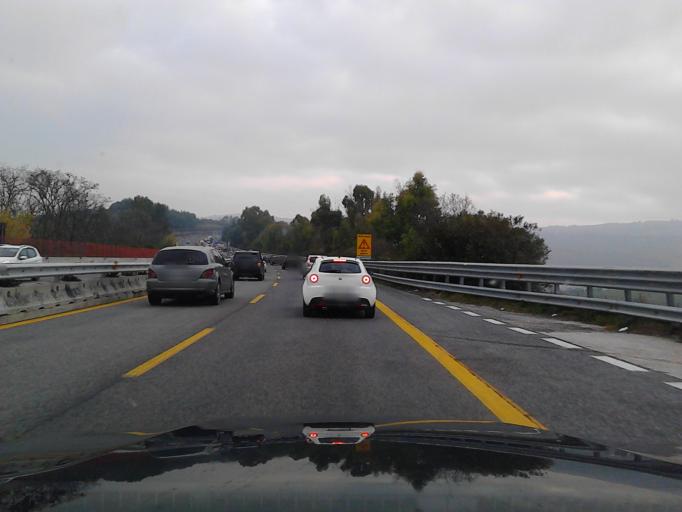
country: IT
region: Abruzzo
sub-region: Provincia di Teramo
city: Tortoreto Lido
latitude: 42.7903
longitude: 13.9340
